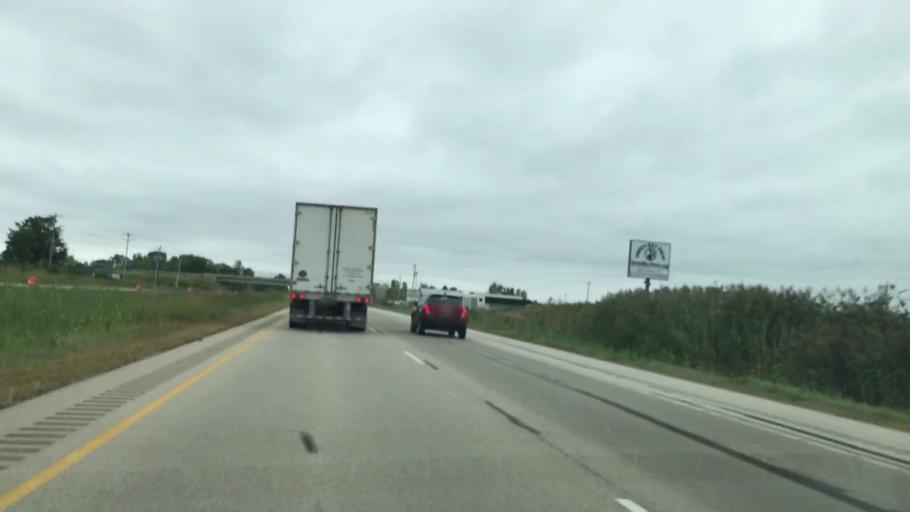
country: US
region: Wisconsin
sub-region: Brown County
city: Suamico
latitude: 44.6655
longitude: -88.0503
